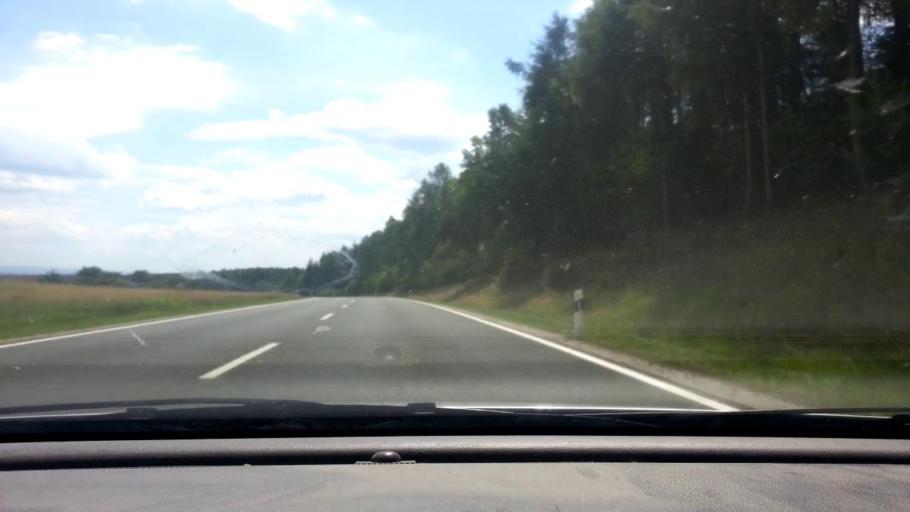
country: DE
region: Bavaria
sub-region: Upper Palatinate
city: Erbendorf
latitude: 49.8391
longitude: 12.0087
